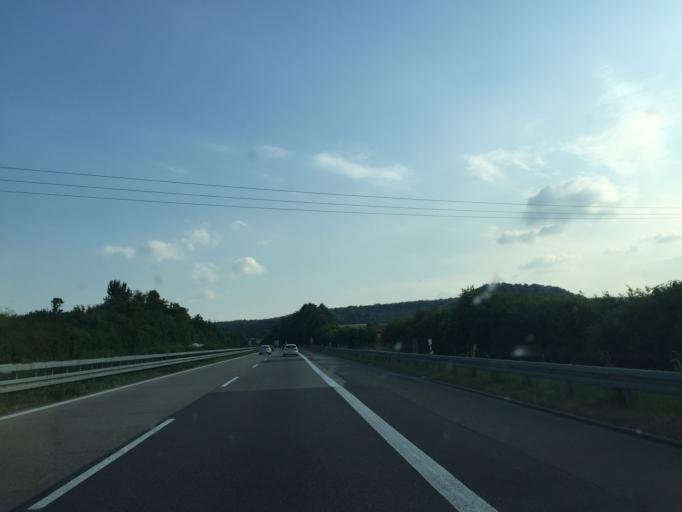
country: DE
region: Baden-Wuerttemberg
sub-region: Regierungsbezirk Stuttgart
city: Neuenstadt am Kocher
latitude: 49.2166
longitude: 9.3475
